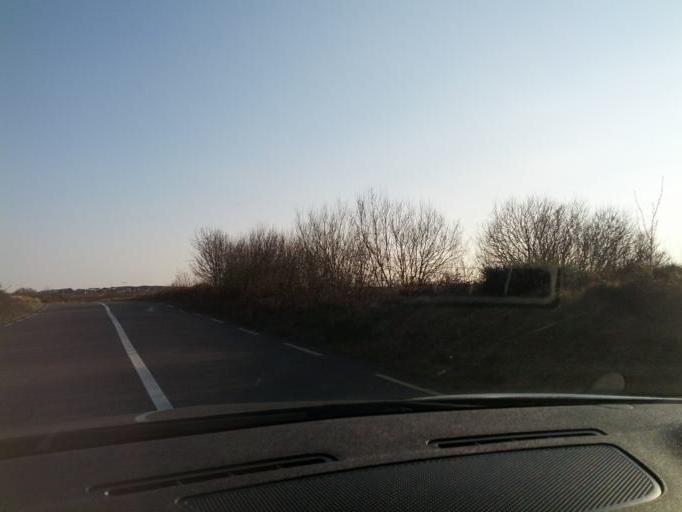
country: IE
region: Connaught
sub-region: County Galway
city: Oughterard
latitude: 53.3076
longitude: -9.5552
